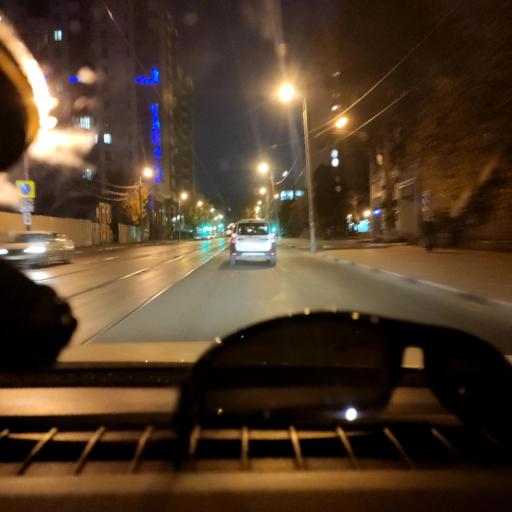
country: RU
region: Samara
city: Samara
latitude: 53.2041
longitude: 50.1179
